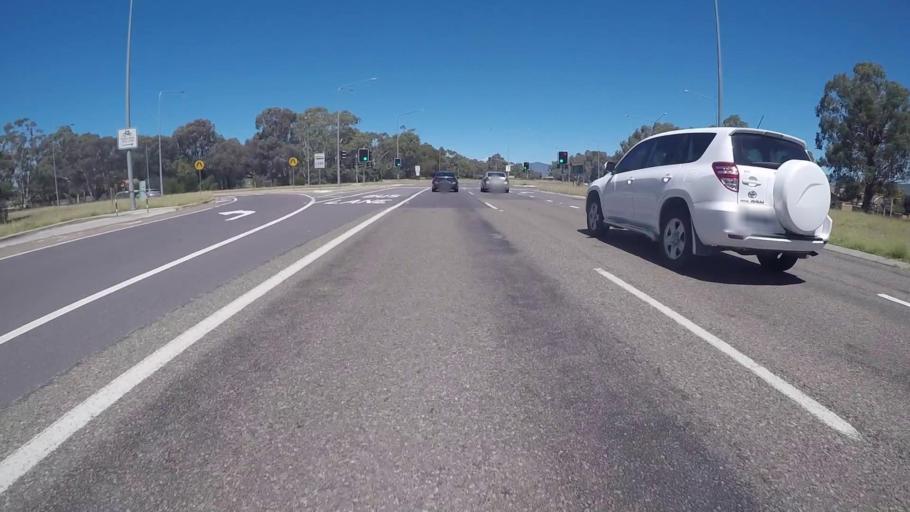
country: AU
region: Australian Capital Territory
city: Macarthur
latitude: -35.4025
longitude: 149.0747
